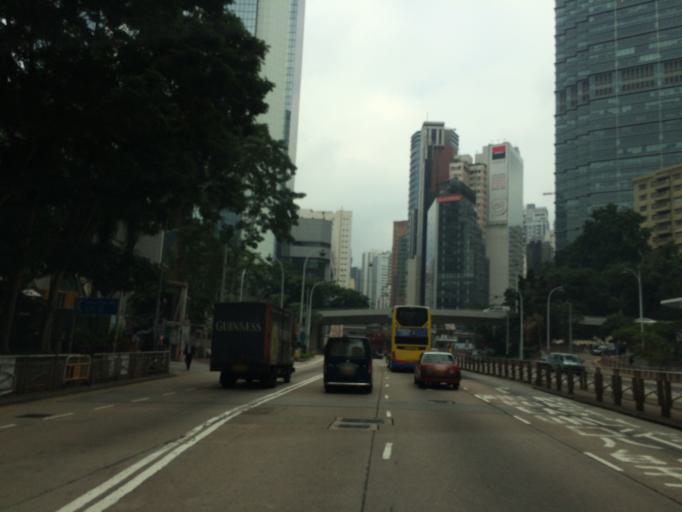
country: HK
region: Wanchai
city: Wan Chai
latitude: 22.2782
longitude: 114.1659
